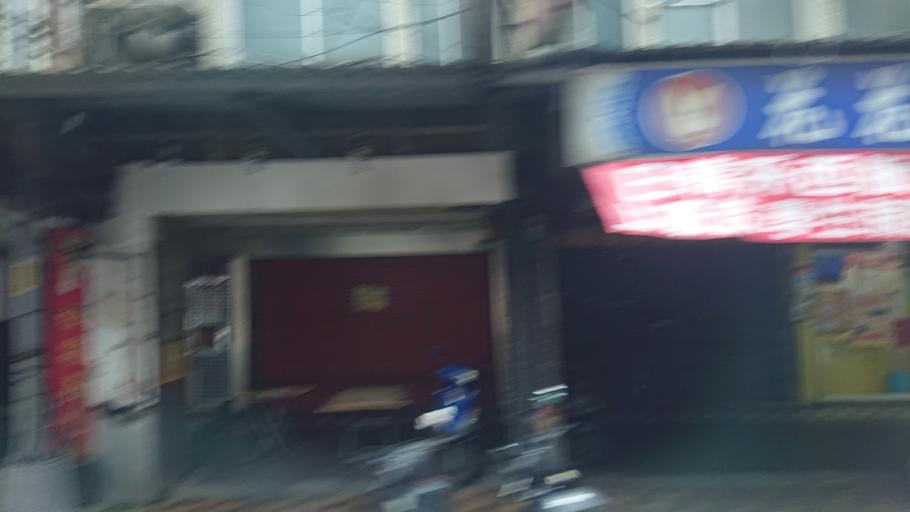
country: TW
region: Taipei
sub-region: Taipei
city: Banqiao
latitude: 25.0061
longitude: 121.4560
